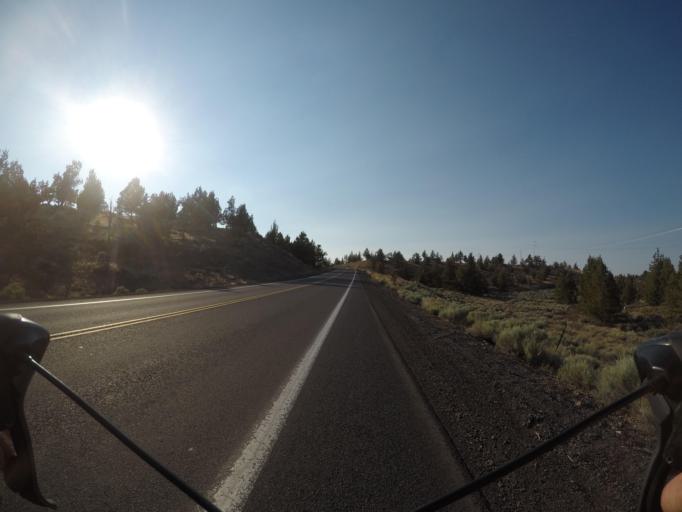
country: US
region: Oregon
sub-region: Deschutes County
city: Redmond
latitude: 44.2722
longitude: -121.2605
